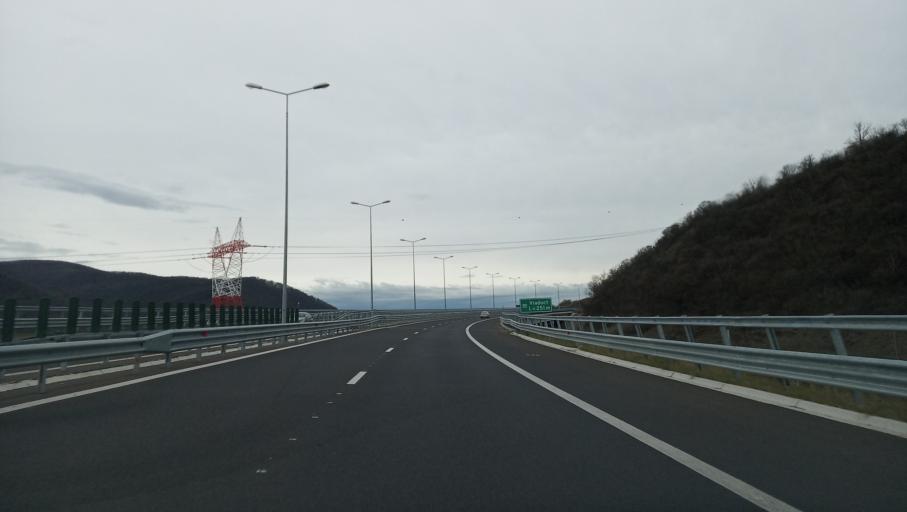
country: RO
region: Hunedoara
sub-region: Comuna Branisca
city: Branisca
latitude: 45.9111
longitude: 22.7905
